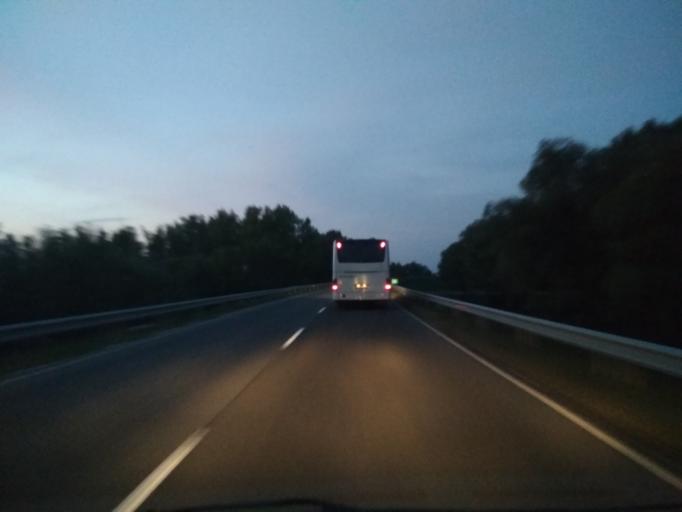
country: HU
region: Fejer
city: Adony
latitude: 47.1465
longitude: 18.8593
